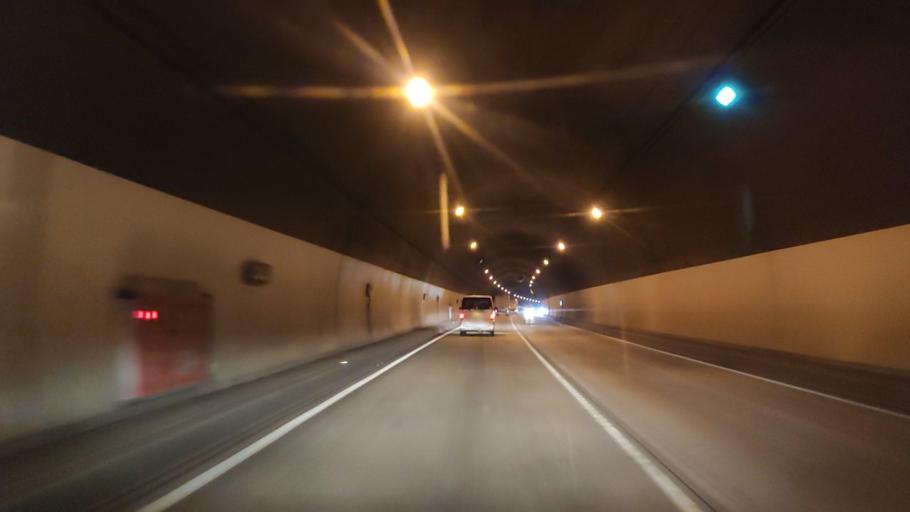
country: JP
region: Yamagata
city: Kaminoyama
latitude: 38.0999
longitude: 140.2041
